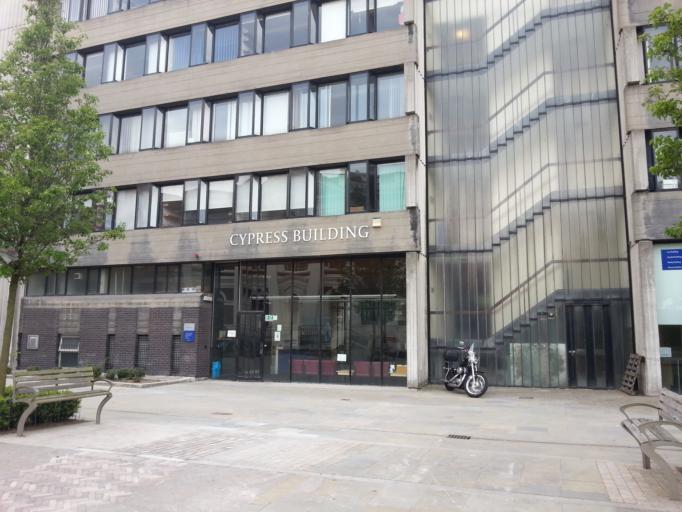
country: GB
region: England
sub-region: Liverpool
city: Liverpool
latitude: 53.4018
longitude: -2.9641
